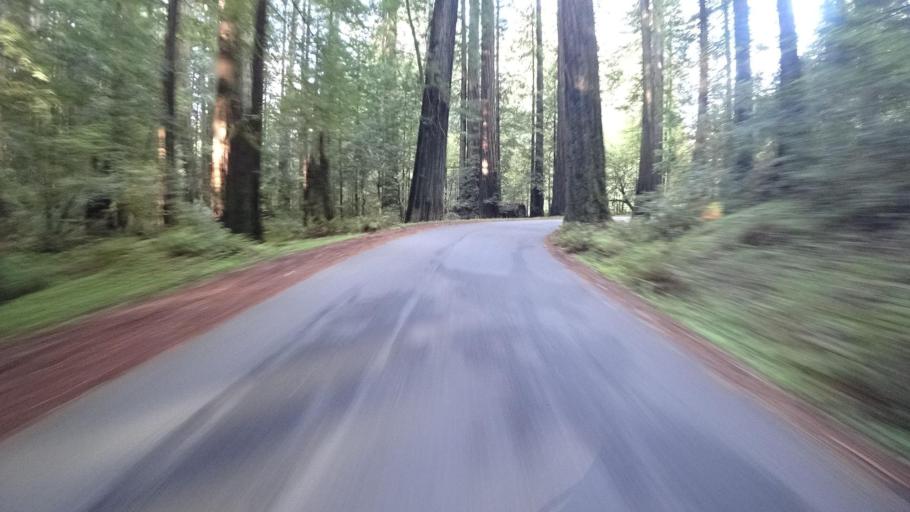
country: US
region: California
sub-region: Humboldt County
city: Rio Dell
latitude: 40.3515
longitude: -123.9768
